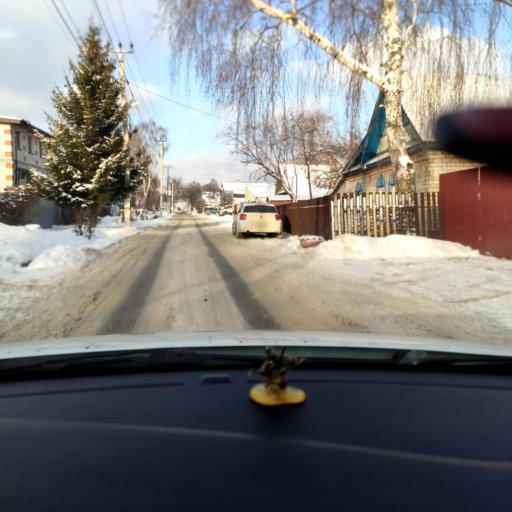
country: RU
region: Tatarstan
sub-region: Gorod Kazan'
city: Kazan
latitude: 55.8810
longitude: 49.0847
